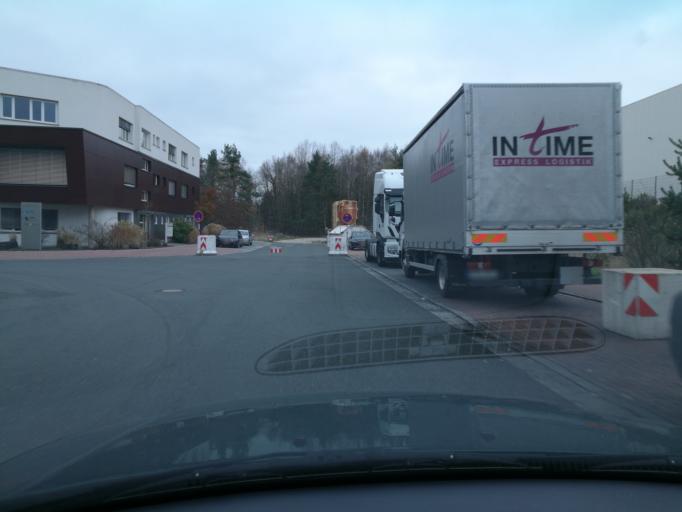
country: DE
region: Bavaria
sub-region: Regierungsbezirk Mittelfranken
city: Feucht
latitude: 49.3855
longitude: 11.1750
